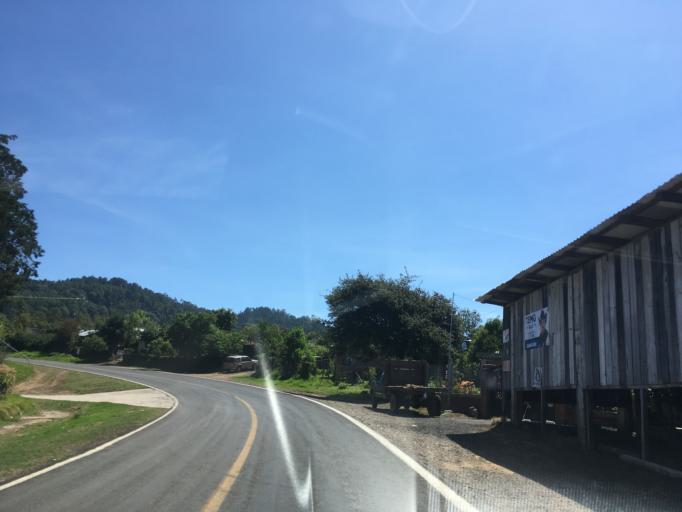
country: MX
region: Michoacan
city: Tzitzio
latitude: 19.6740
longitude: -100.8513
